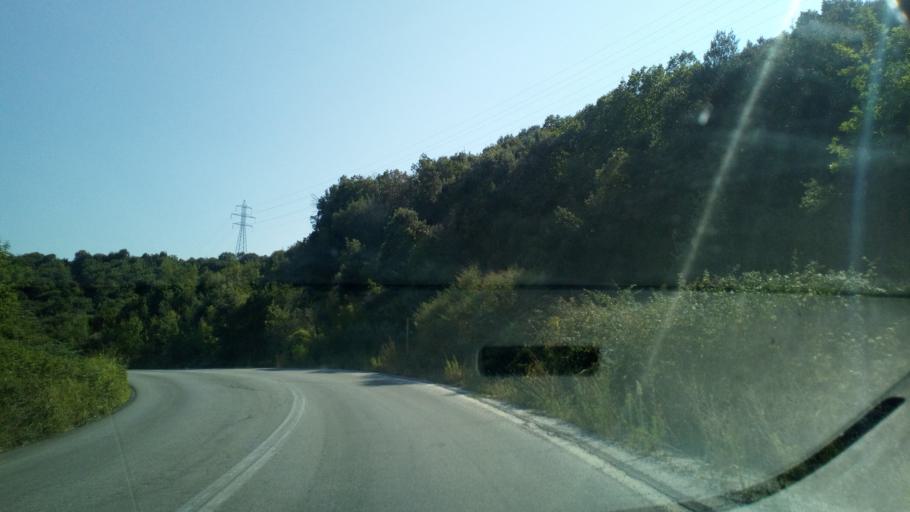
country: GR
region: Central Macedonia
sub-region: Nomos Thessalonikis
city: Stavros
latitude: 40.6538
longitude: 23.7399
